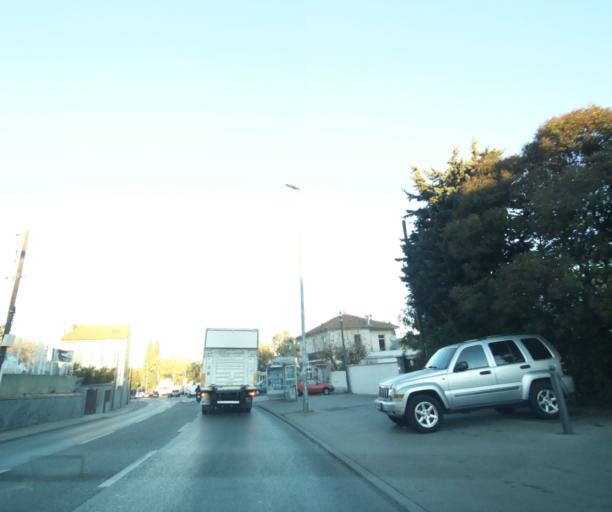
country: FR
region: Provence-Alpes-Cote d'Azur
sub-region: Departement des Bouches-du-Rhone
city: Marseille 12
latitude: 43.3253
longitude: 5.4418
